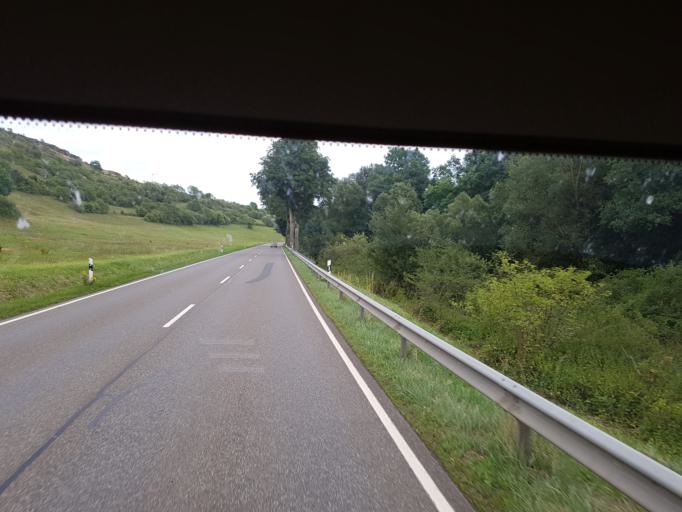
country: DE
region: Rheinland-Pfalz
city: Kalenborn-Scheuern
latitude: 50.2220
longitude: 6.6182
